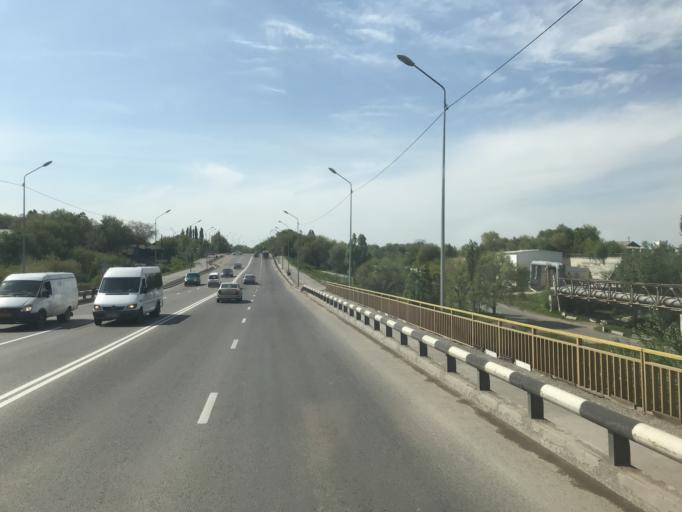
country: KZ
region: Almaty Oblysy
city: Burunday
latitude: 43.3103
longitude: 76.8692
